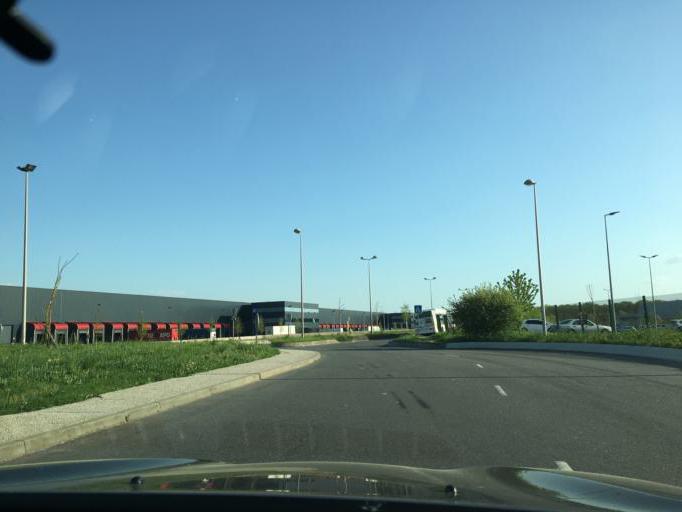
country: FR
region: Centre
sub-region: Departement du Loiret
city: Gidy
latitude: 47.9637
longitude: 1.8474
